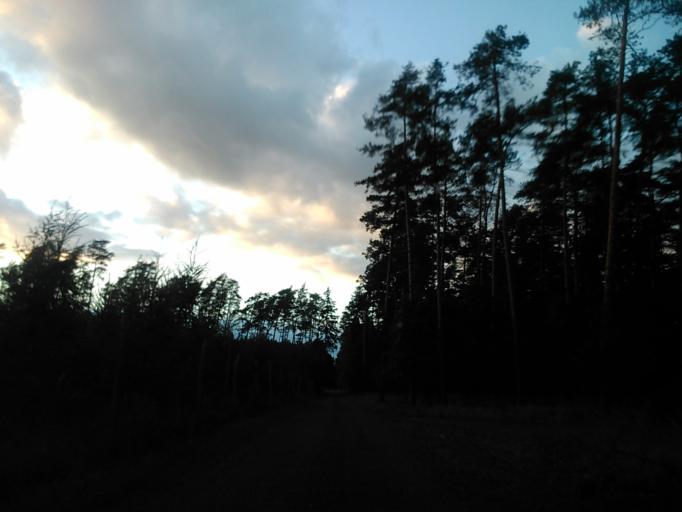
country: PL
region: Kujawsko-Pomorskie
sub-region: Powiat wabrzeski
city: Debowa Laka
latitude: 53.1677
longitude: 19.1363
